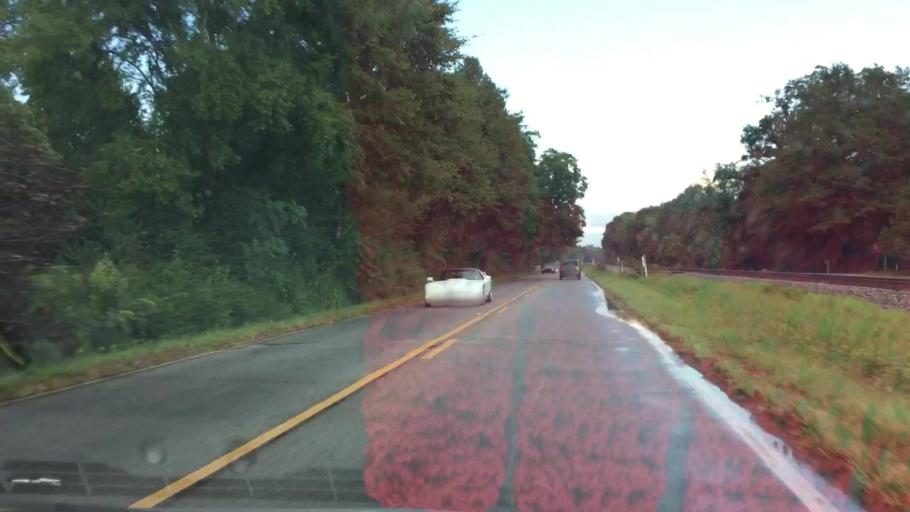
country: US
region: Georgia
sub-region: Clayton County
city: Lovejoy
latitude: 33.4334
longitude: -84.3030
